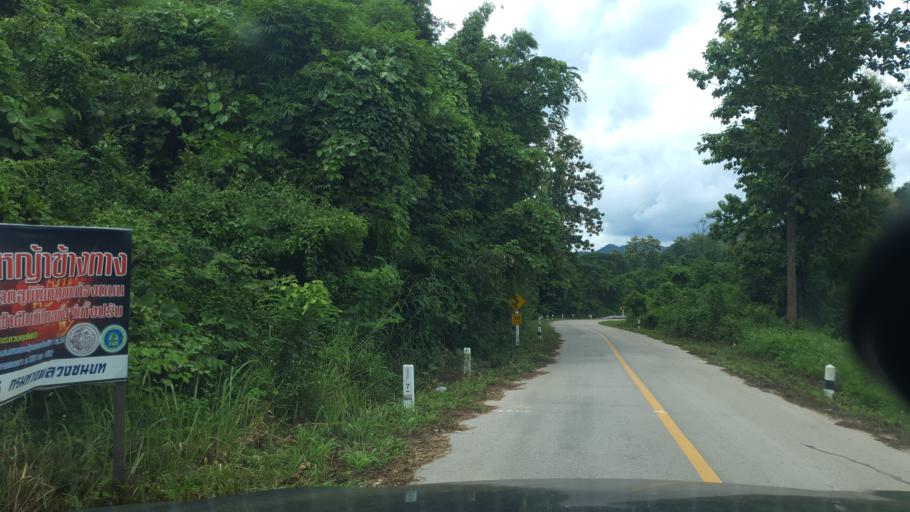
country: TH
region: Lampang
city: Hang Chat
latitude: 18.3659
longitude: 99.2603
